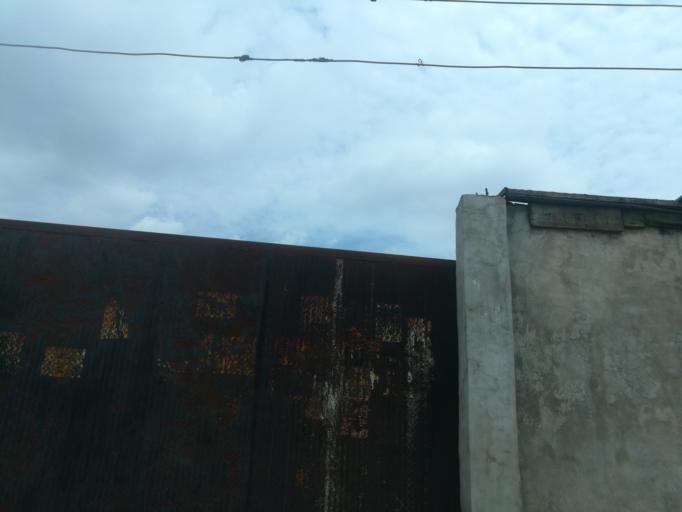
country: NG
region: Lagos
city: Ojota
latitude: 6.5734
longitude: 3.3673
